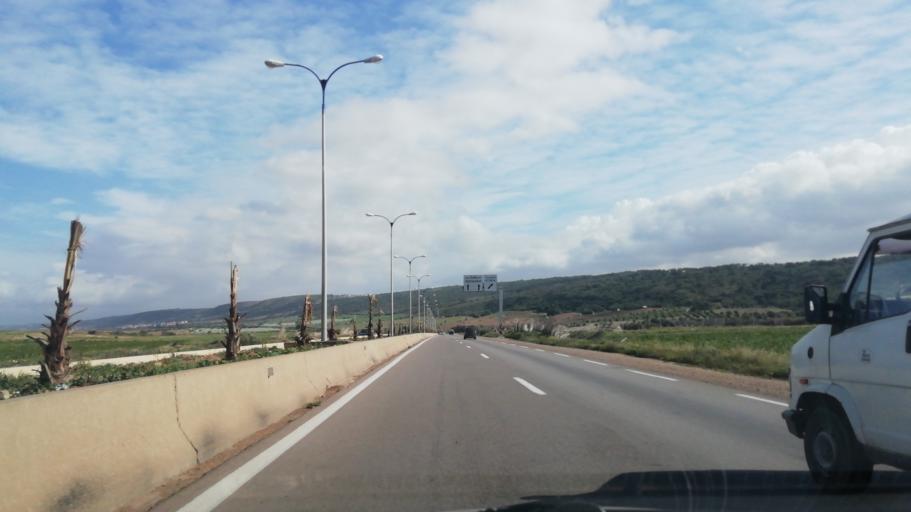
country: DZ
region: Mostaganem
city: Mostaganem
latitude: 35.8391
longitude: 0.0043
